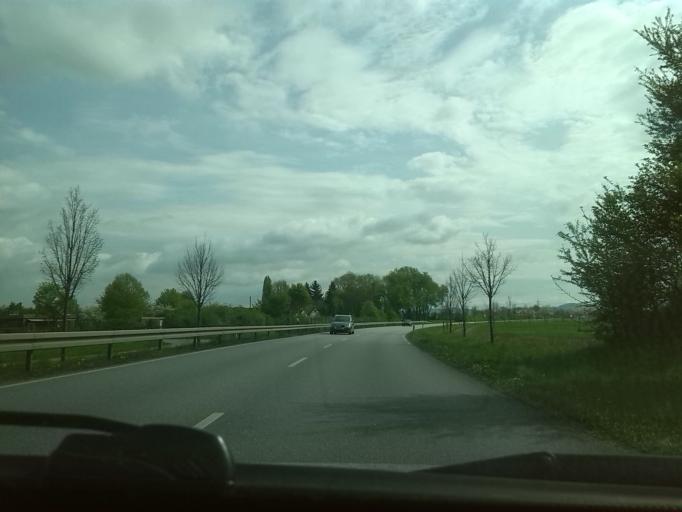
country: DE
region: Hesse
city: Pfungstadt
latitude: 49.8003
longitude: 8.5499
